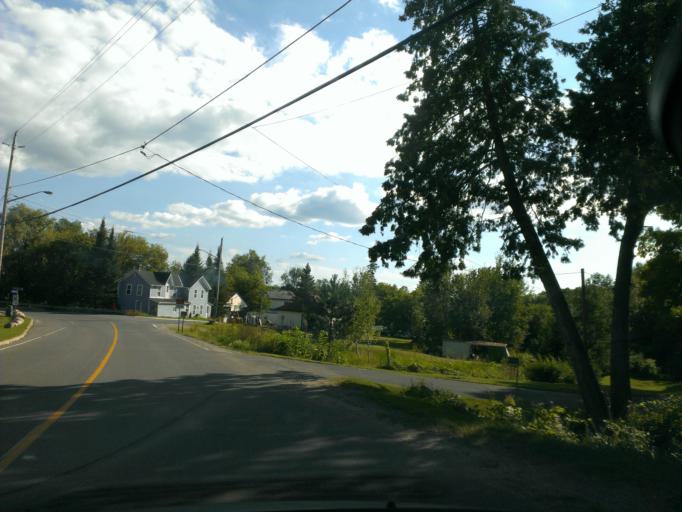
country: CA
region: Ontario
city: Skatepark
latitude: 44.7231
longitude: -76.9250
